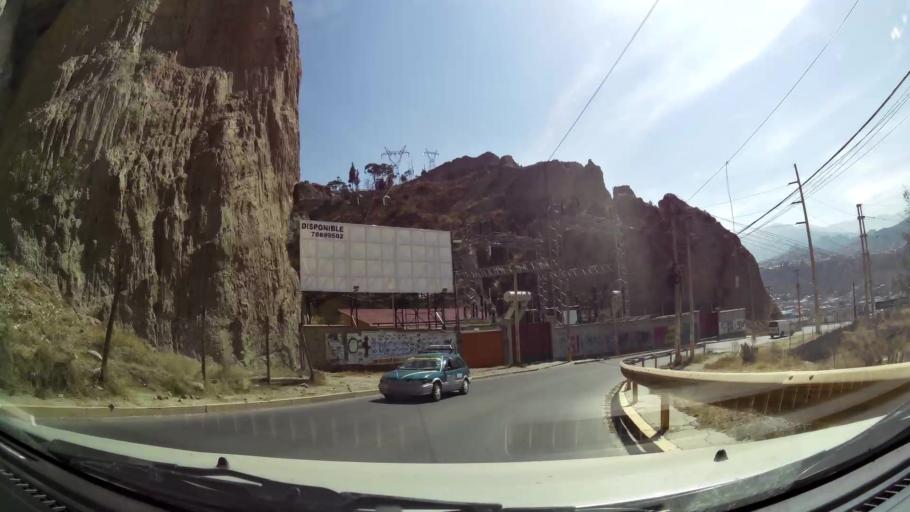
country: BO
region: La Paz
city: La Paz
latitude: -16.5259
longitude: -68.0938
